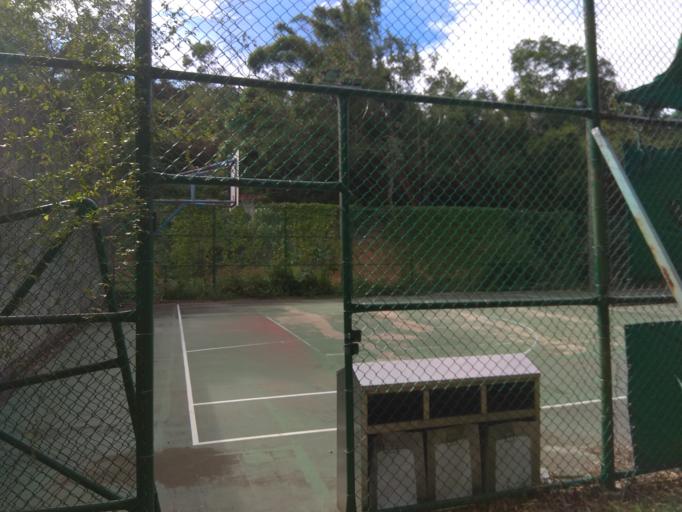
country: TW
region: Taiwan
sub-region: Hsinchu
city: Hsinchu
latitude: 24.7622
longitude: 120.9553
